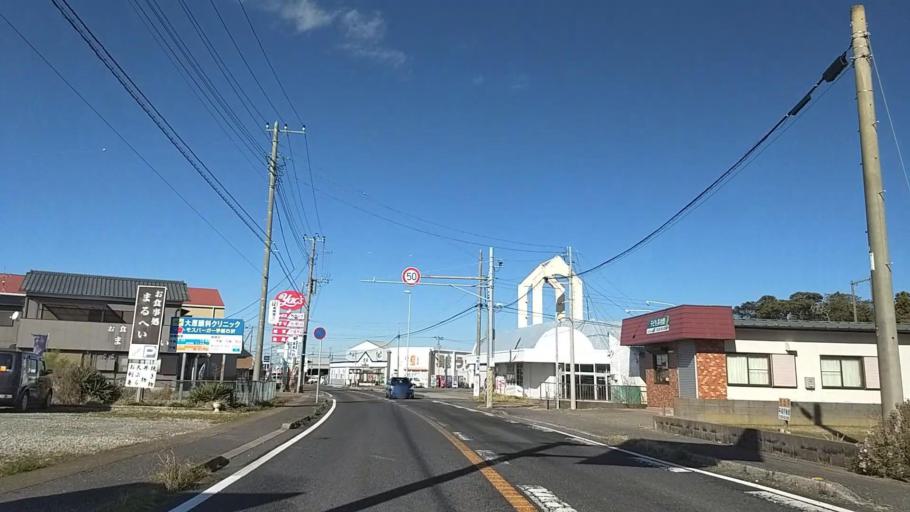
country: JP
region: Chiba
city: Ohara
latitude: 35.2514
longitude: 140.3962
